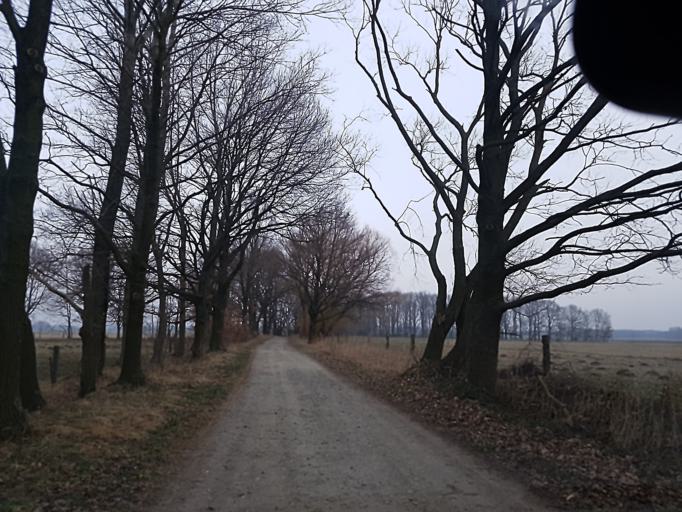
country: DE
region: Brandenburg
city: Ruckersdorf
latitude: 51.5762
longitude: 13.5423
